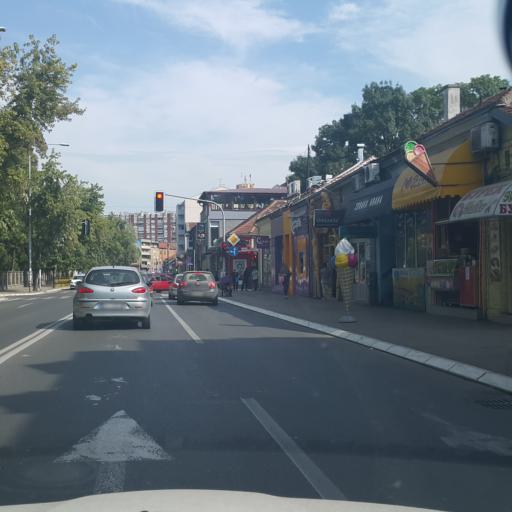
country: RS
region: Central Serbia
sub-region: Nisavski Okrug
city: Nis
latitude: 43.3203
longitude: 21.9025
